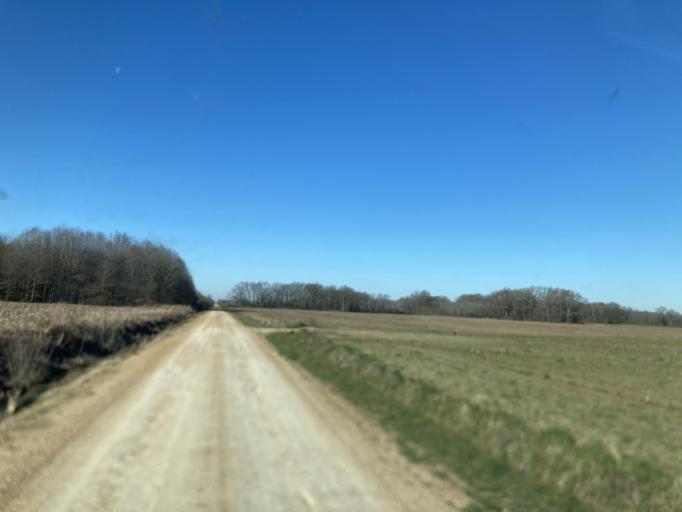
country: US
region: Mississippi
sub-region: Yazoo County
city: Yazoo City
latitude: 32.9519
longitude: -90.6098
